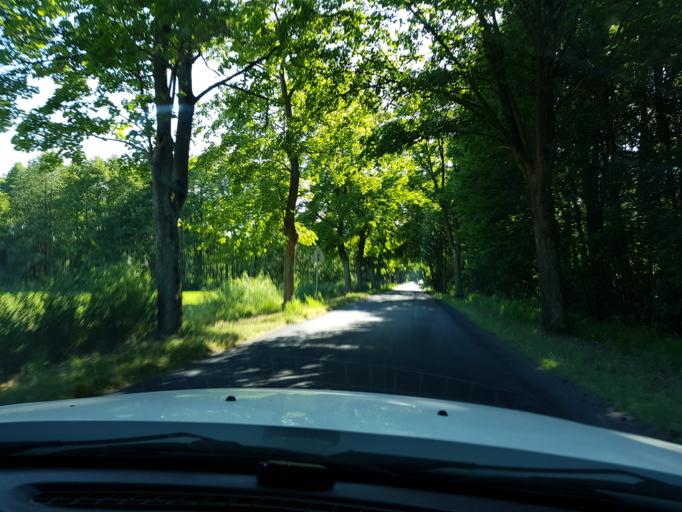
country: PL
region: West Pomeranian Voivodeship
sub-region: Powiat bialogardzki
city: Bialogard
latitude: 53.9918
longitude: 15.9516
